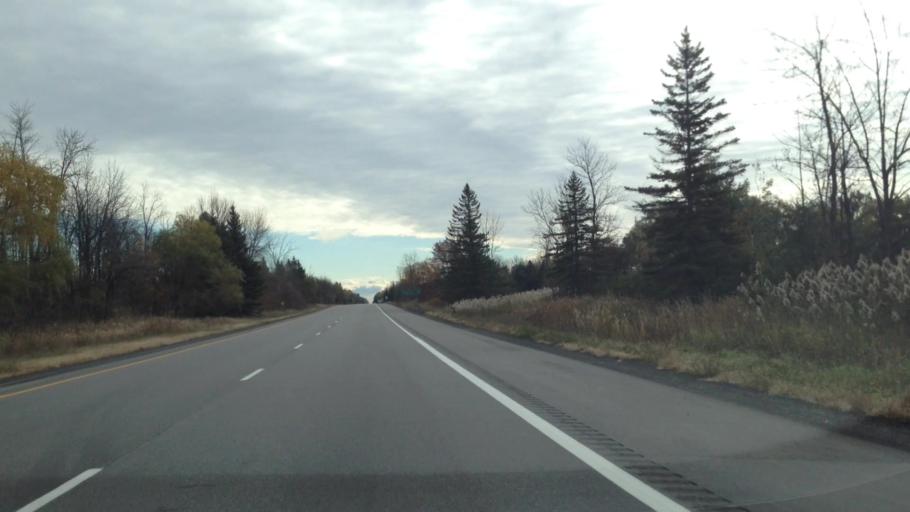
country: CA
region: Ontario
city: Hawkesbury
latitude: 45.5629
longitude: -74.4897
